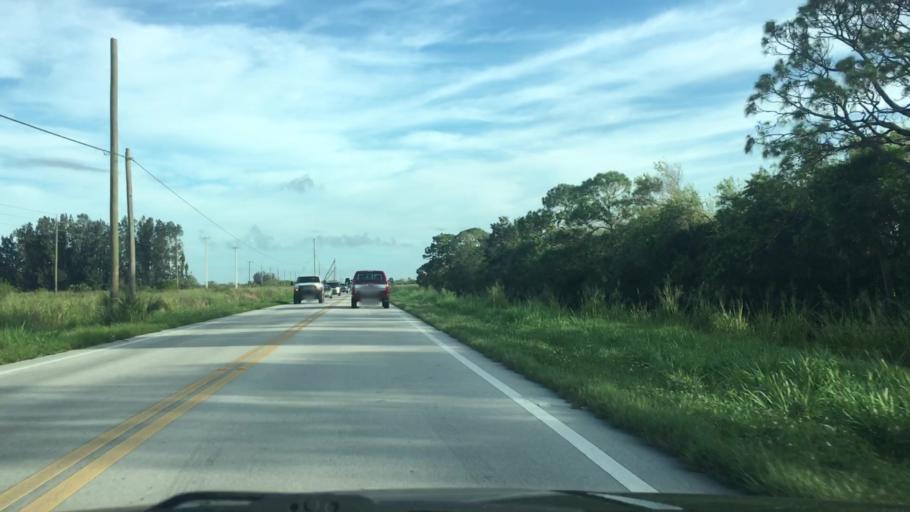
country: US
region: Florida
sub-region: Indian River County
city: Winter Beach
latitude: 27.6908
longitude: -80.4627
